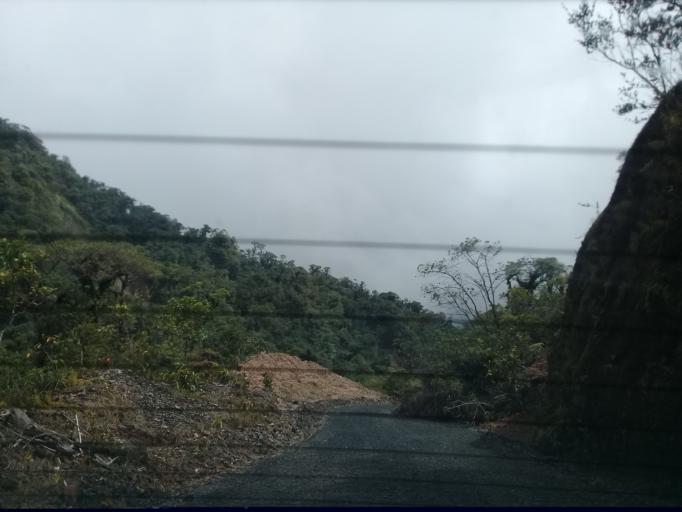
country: CO
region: Cundinamarca
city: Gachala
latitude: 4.7006
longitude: -73.4170
